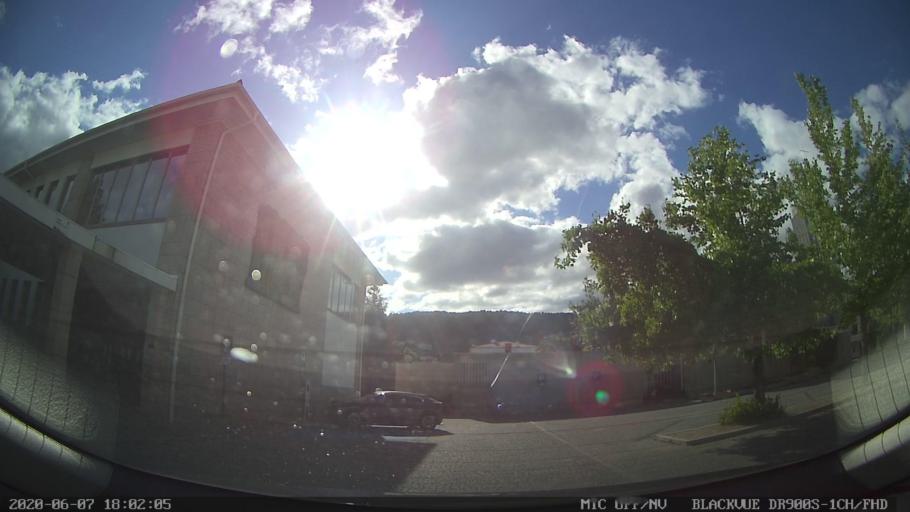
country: PT
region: Vila Real
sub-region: Vila Pouca de Aguiar
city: Vila Pouca de Aguiar
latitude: 41.4989
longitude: -7.6436
